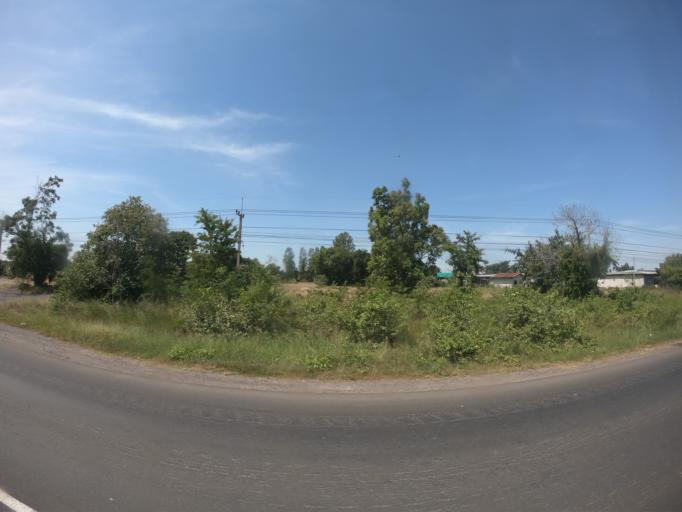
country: TH
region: Nakhon Ratchasima
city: Sida
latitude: 15.6050
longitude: 102.5620
